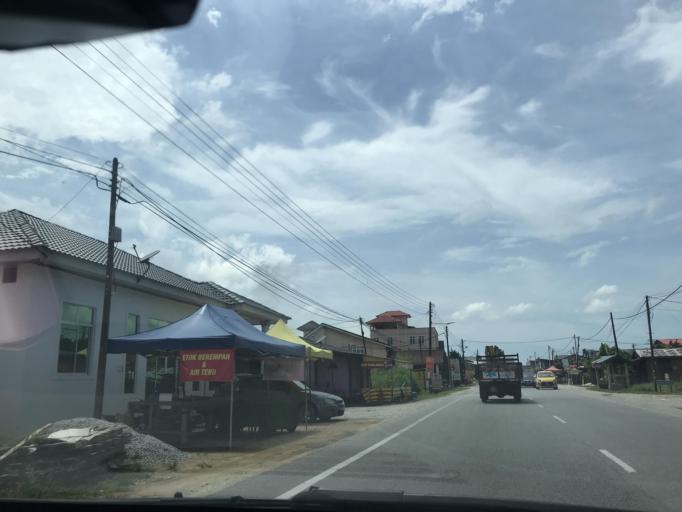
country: MY
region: Kelantan
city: Kota Bharu
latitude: 6.0931
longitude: 102.2298
